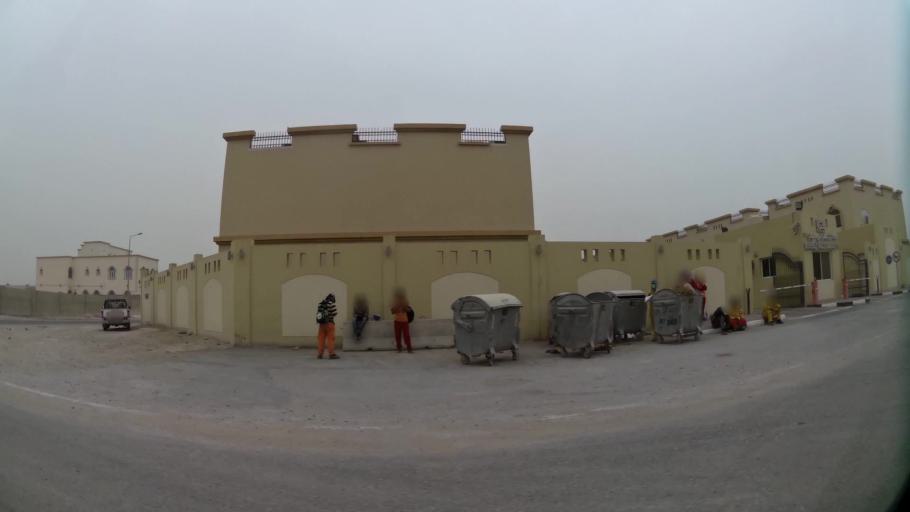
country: QA
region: Baladiyat ad Dawhah
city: Doha
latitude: 25.2448
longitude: 51.4869
